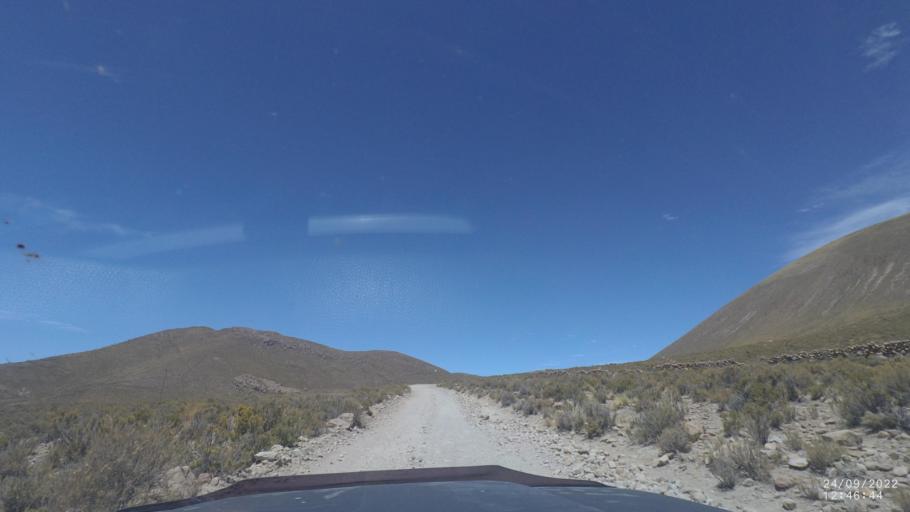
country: BO
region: Potosi
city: Colchani
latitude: -19.8052
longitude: -67.5703
